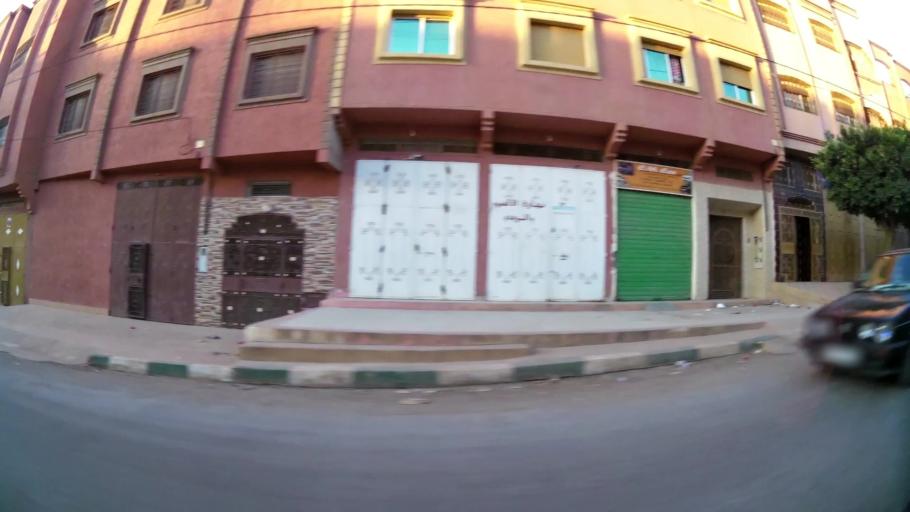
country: MA
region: Oriental
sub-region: Berkane-Taourirt
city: Berkane
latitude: 34.9128
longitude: -2.3190
